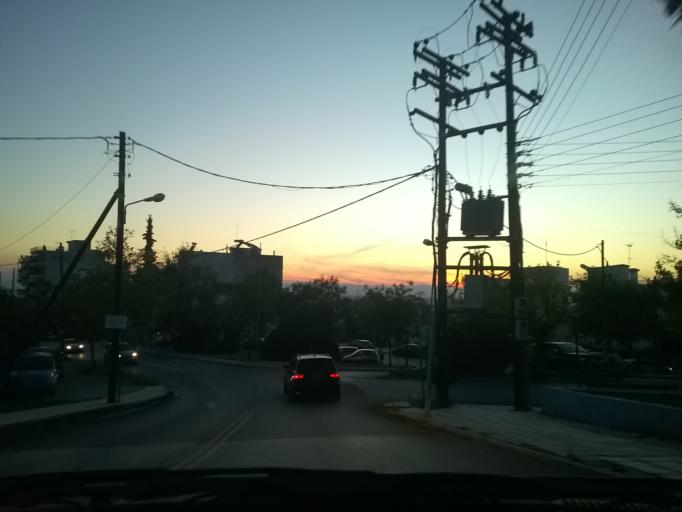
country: GR
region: Central Macedonia
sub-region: Nomos Thessalonikis
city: Polichni
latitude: 40.6652
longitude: 22.9502
